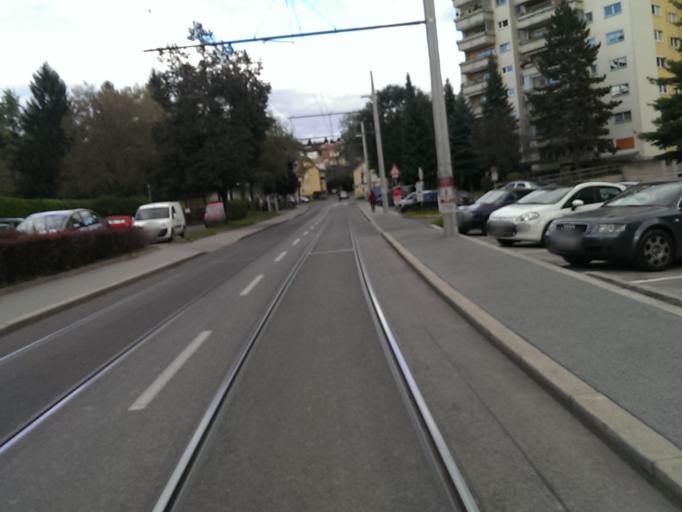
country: AT
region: Styria
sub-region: Graz Stadt
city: Graz
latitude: 47.0611
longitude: 15.4707
